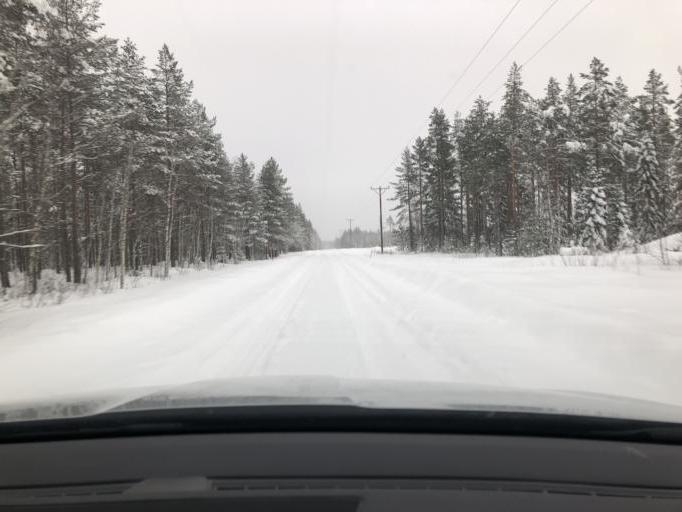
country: SE
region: Vaesterbotten
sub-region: Umea Kommun
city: Saevar
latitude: 63.9483
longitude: 20.6890
